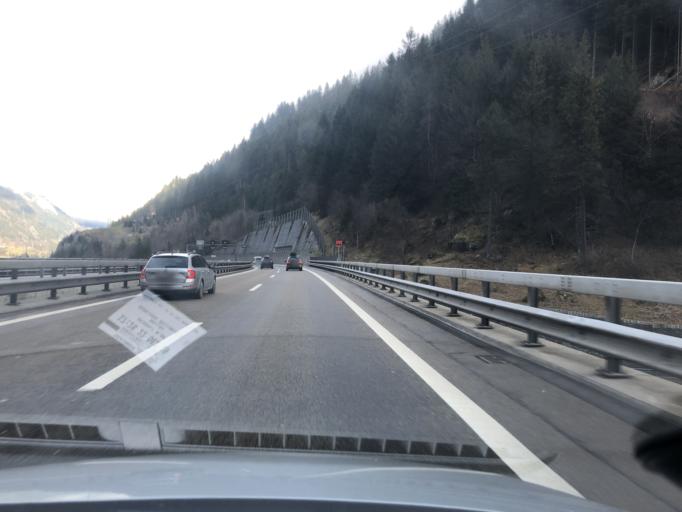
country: CH
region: Uri
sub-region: Uri
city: Andermatt
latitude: 46.6881
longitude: 8.5919
